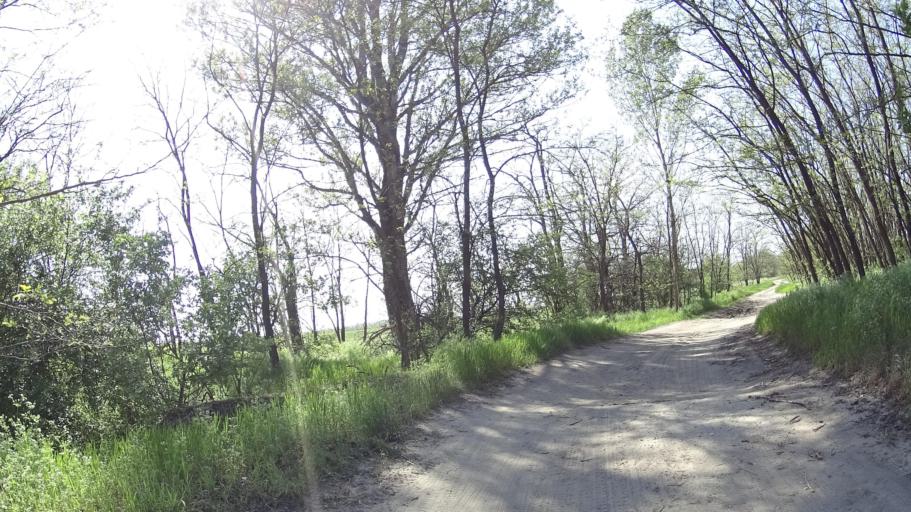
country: HU
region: Pest
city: Vecses
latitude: 47.4343
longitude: 19.2863
